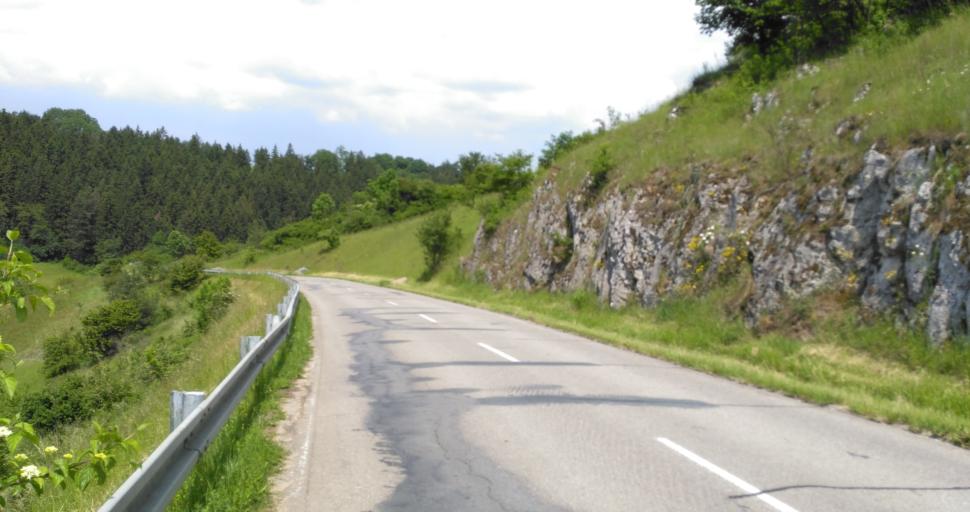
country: CZ
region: South Moravian
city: Ostrov u Macochy
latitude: 49.3683
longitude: 16.7430
